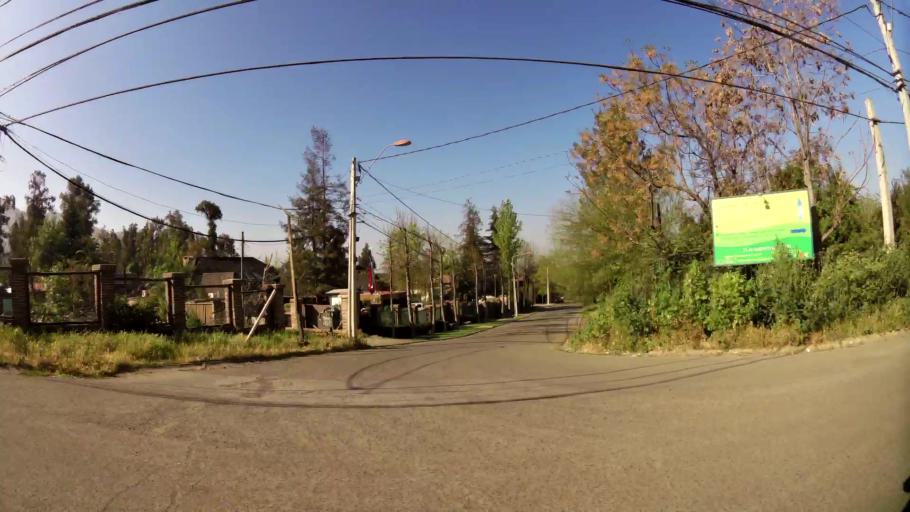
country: CL
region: Santiago Metropolitan
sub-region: Provincia de Chacabuco
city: Chicureo Abajo
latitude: -33.3397
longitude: -70.6704
